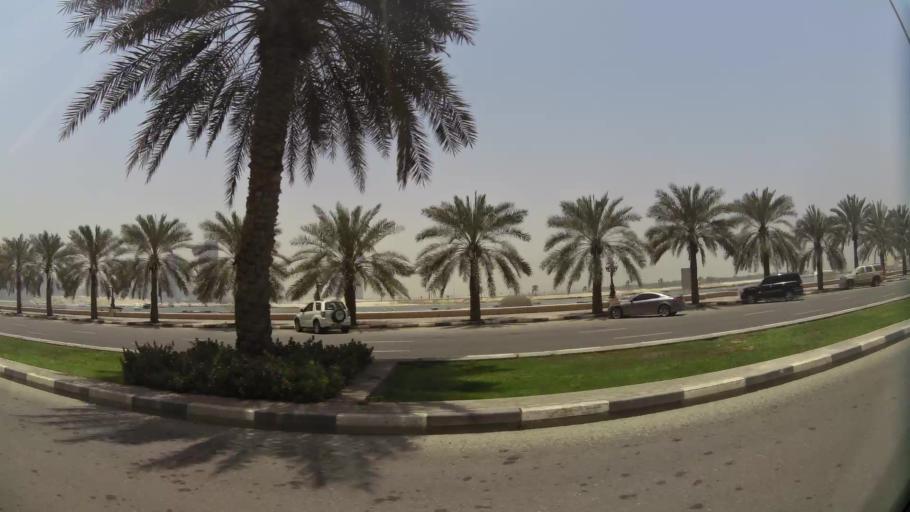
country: AE
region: Ash Shariqah
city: Sharjah
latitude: 25.3308
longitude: 55.3629
